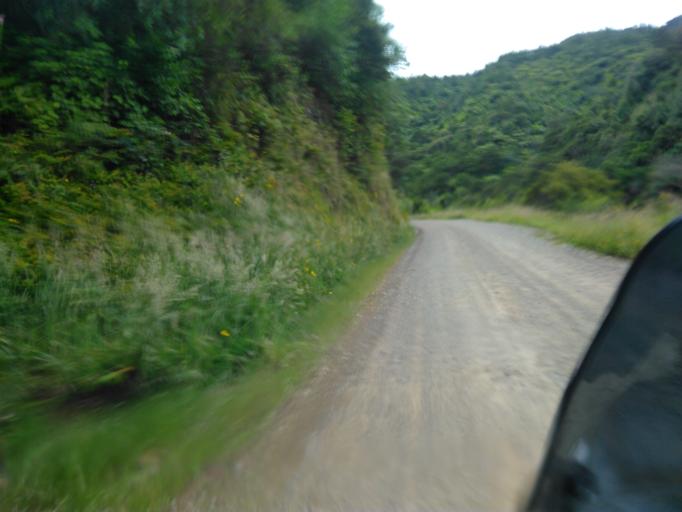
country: NZ
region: Bay of Plenty
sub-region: Opotiki District
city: Opotiki
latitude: -38.0352
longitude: 177.4421
